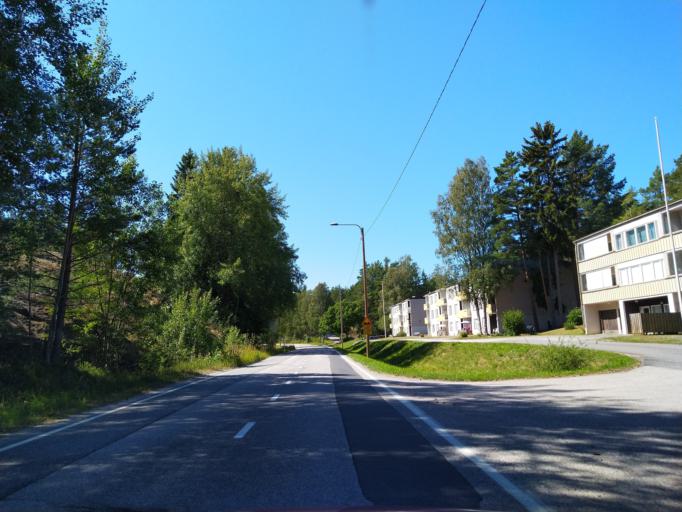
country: FI
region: Varsinais-Suomi
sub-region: Aboland-Turunmaa
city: Dragsfjaerd
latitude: 60.0190
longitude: 22.4861
